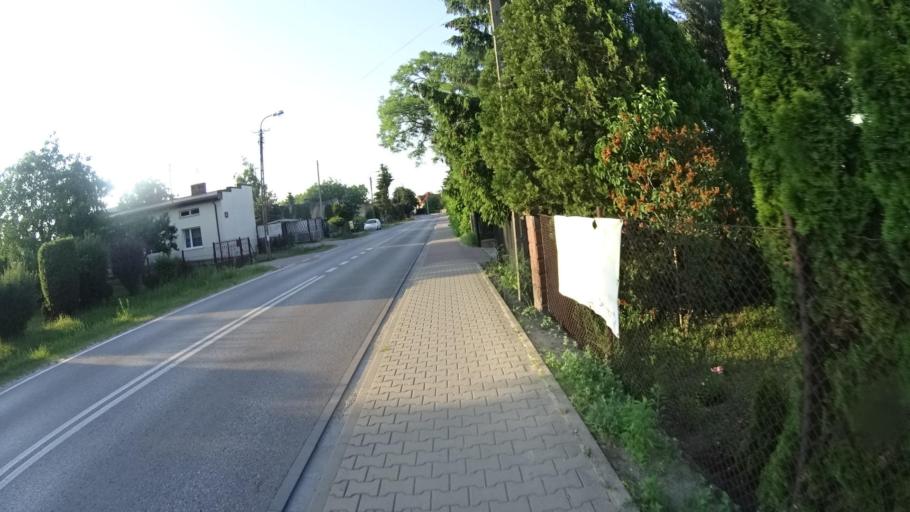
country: PL
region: Masovian Voivodeship
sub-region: Powiat warszawski zachodni
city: Stare Babice
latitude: 52.2537
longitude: 20.8384
